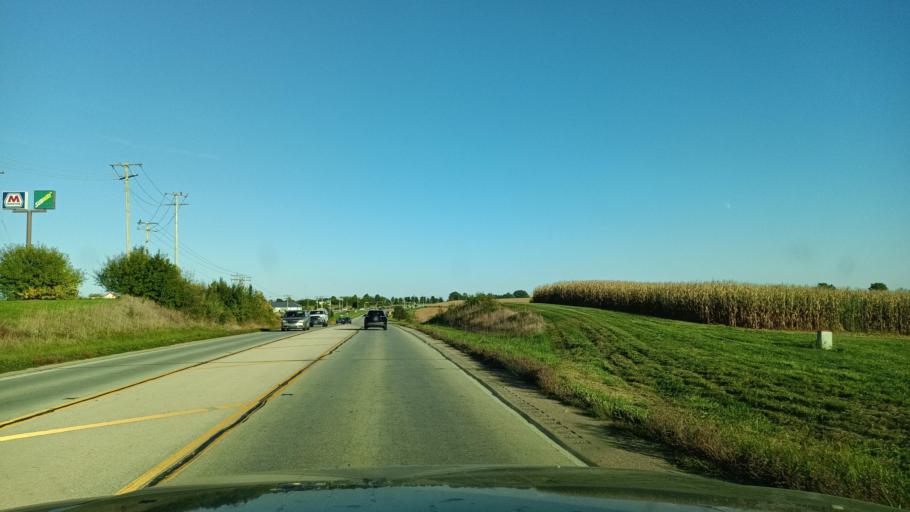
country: US
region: Illinois
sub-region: Champaign County
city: Lake of the Woods
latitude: 40.1854
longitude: -88.3713
